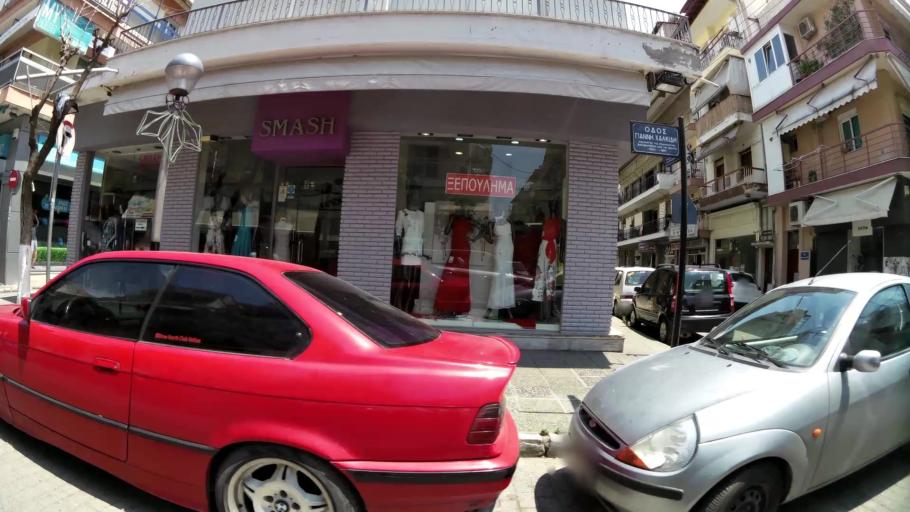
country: GR
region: Central Macedonia
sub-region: Nomos Thessalonikis
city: Ampelokipoi
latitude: 40.6519
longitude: 22.9227
